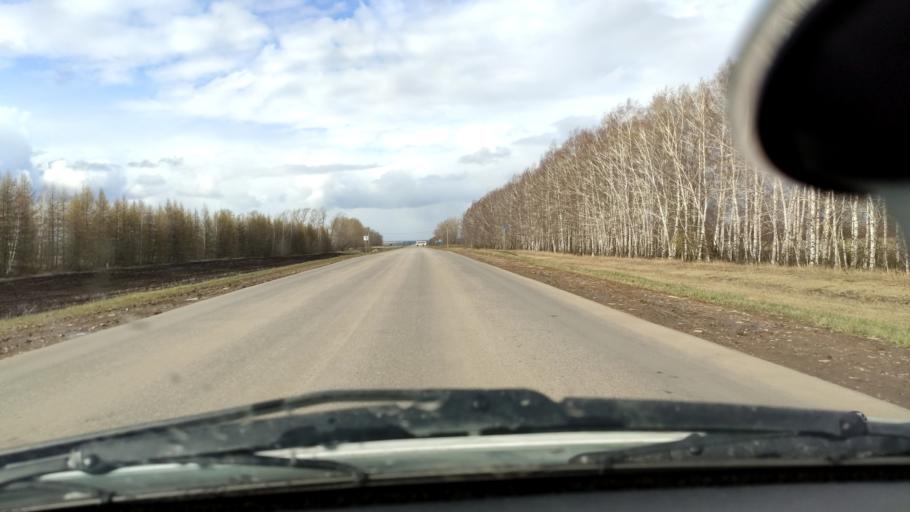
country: RU
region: Bashkortostan
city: Buzdyak
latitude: 54.7050
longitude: 54.5648
